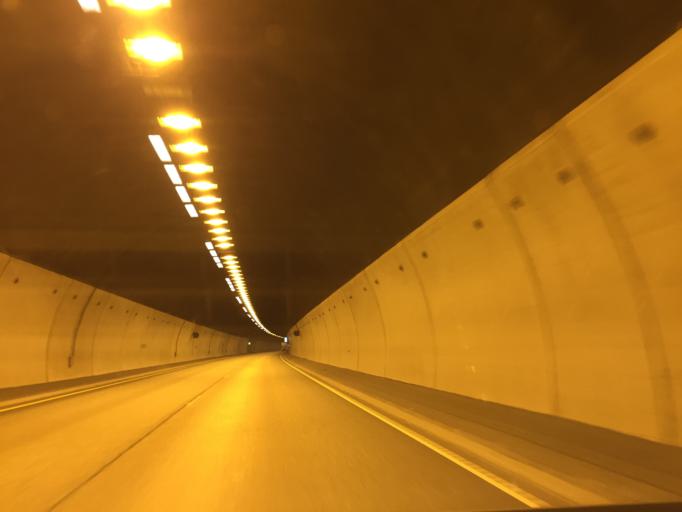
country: NO
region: Vestfold
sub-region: Sande
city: Sande
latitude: 59.5329
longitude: 10.1832
